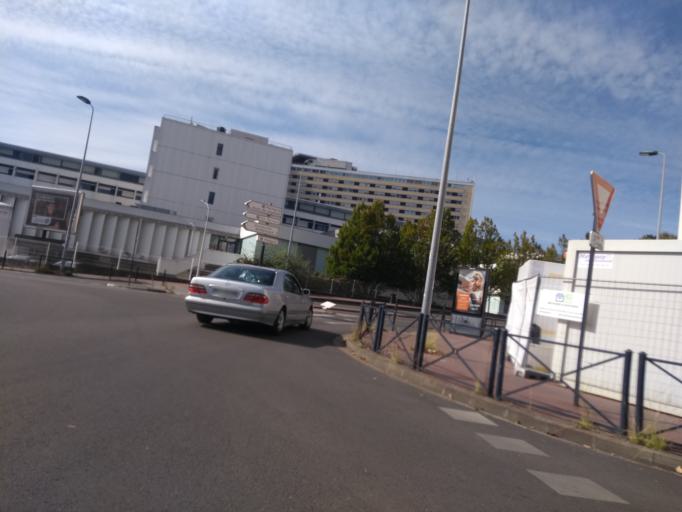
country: FR
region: Aquitaine
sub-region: Departement de la Gironde
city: Talence
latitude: 44.8272
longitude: -0.6014
